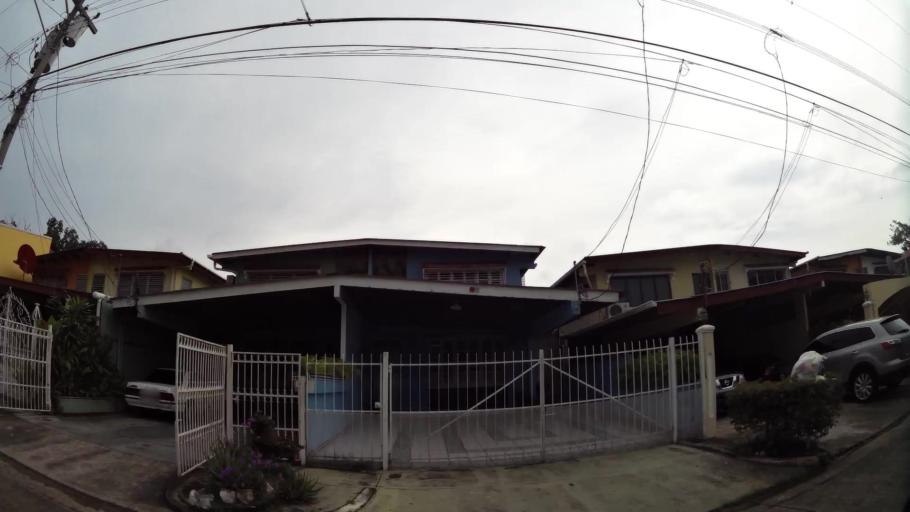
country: PA
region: Panama
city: Panama
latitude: 9.0073
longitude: -79.5296
